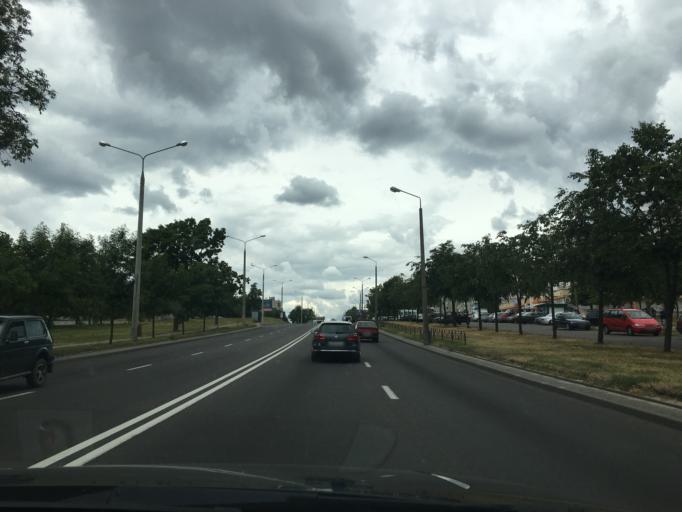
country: BY
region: Grodnenskaya
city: Hrodna
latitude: 53.6427
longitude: 23.8418
